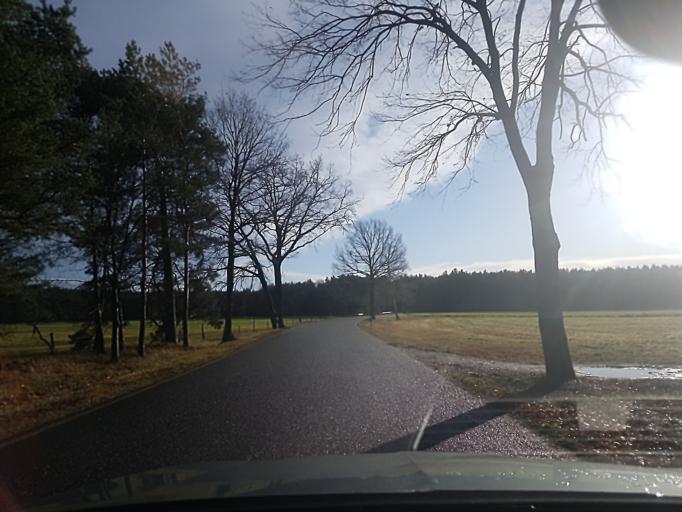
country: DE
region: Brandenburg
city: Schilda
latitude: 51.5720
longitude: 13.3294
